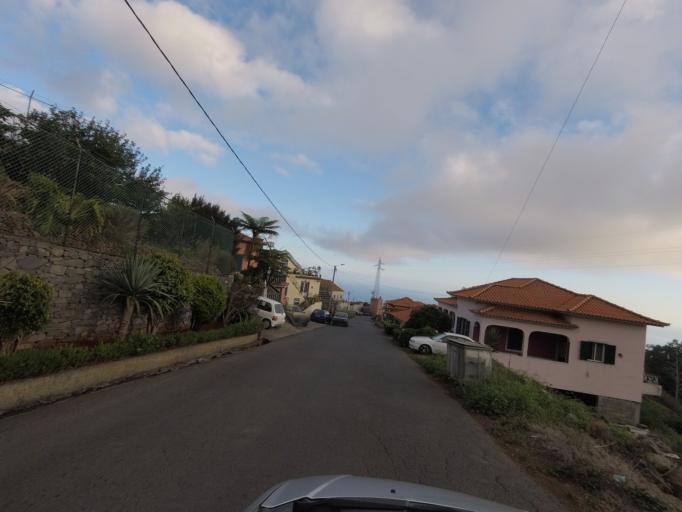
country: PT
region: Madeira
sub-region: Calheta
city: Arco da Calheta
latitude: 32.7105
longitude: -17.1167
